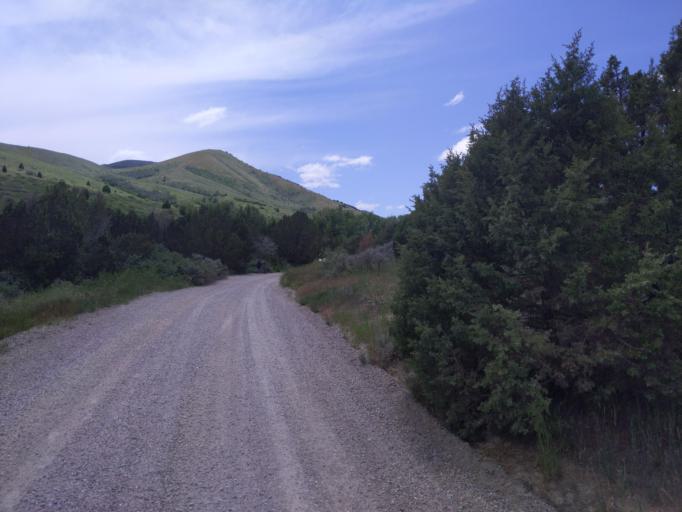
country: US
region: Idaho
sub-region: Bannock County
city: Pocatello
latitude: 42.8418
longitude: -112.4613
